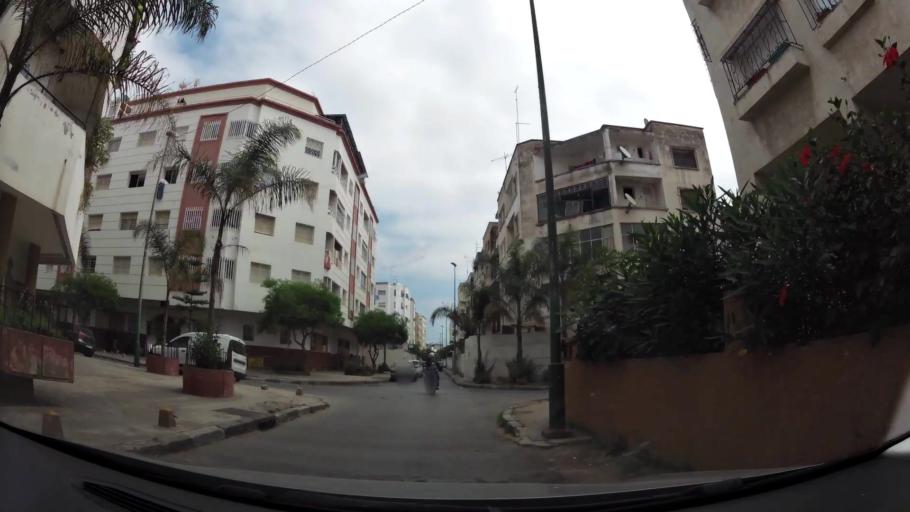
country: MA
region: Rabat-Sale-Zemmour-Zaer
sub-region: Rabat
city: Rabat
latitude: 34.0144
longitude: -6.8496
